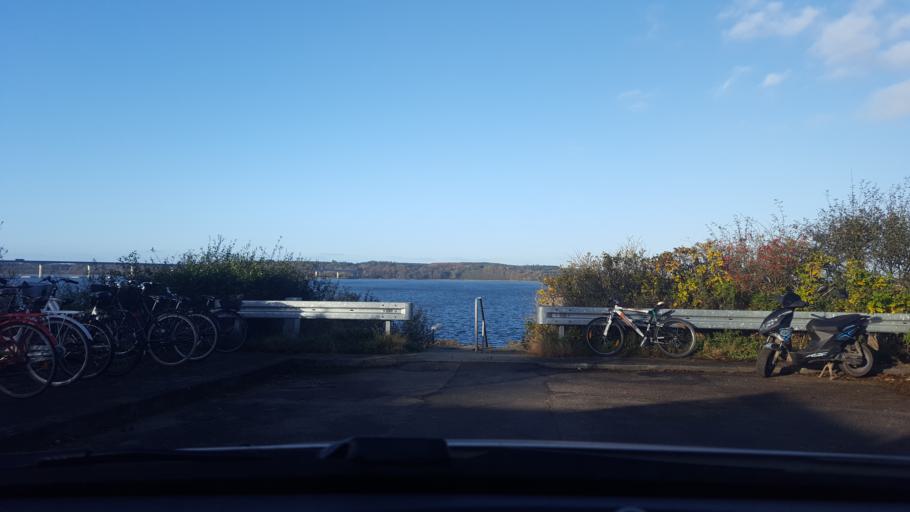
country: DK
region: North Denmark
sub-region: Morso Kommune
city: Nykobing Mors
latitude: 56.7533
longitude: 8.8719
